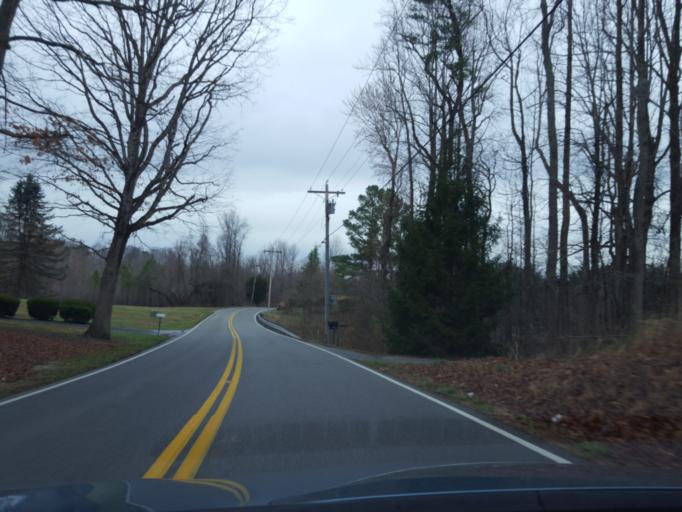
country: US
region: Maryland
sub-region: Calvert County
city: Huntingtown
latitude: 38.6252
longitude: -76.5703
